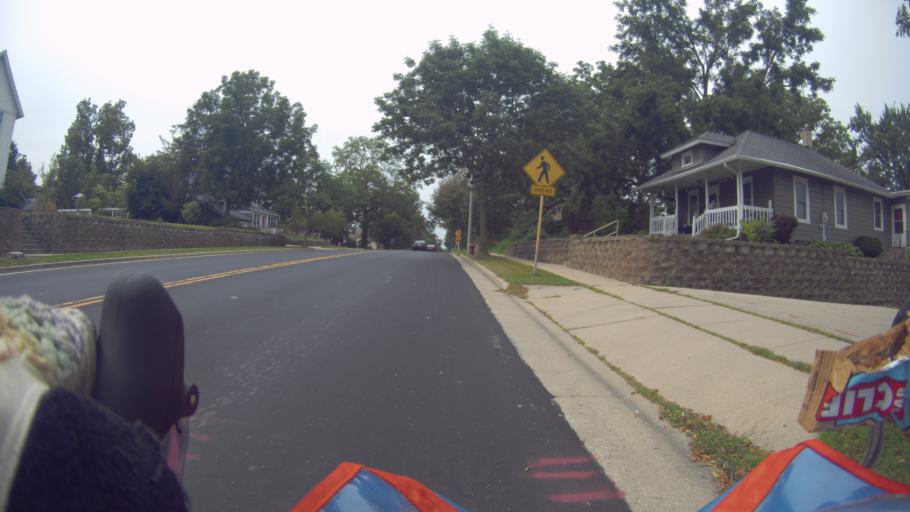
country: US
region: Wisconsin
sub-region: Dane County
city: Verona
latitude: 42.9851
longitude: -89.5348
